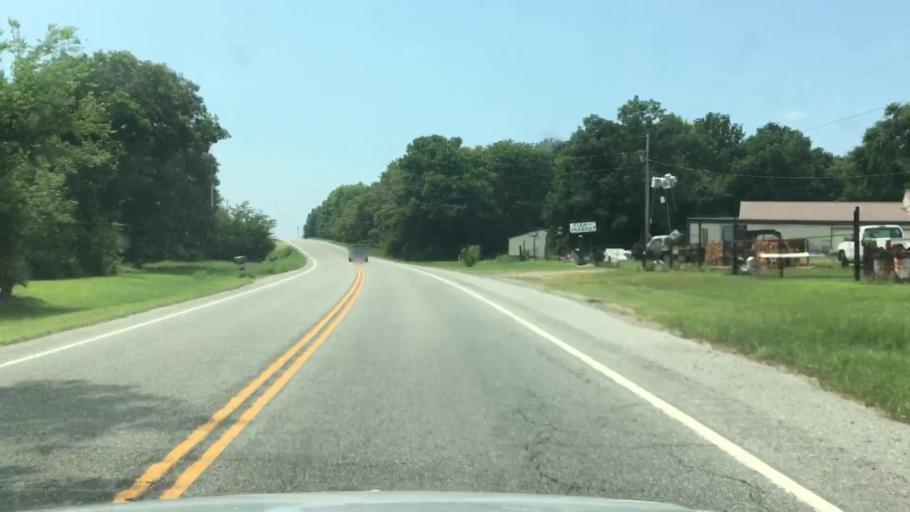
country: US
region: Oklahoma
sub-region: Muskogee County
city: Fort Gibson
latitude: 35.9355
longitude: -95.2275
